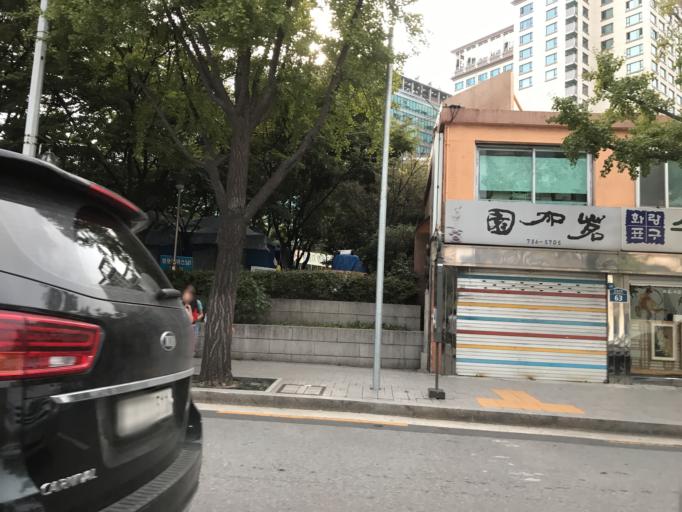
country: KR
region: Seoul
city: Seoul
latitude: 37.5749
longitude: 126.9829
